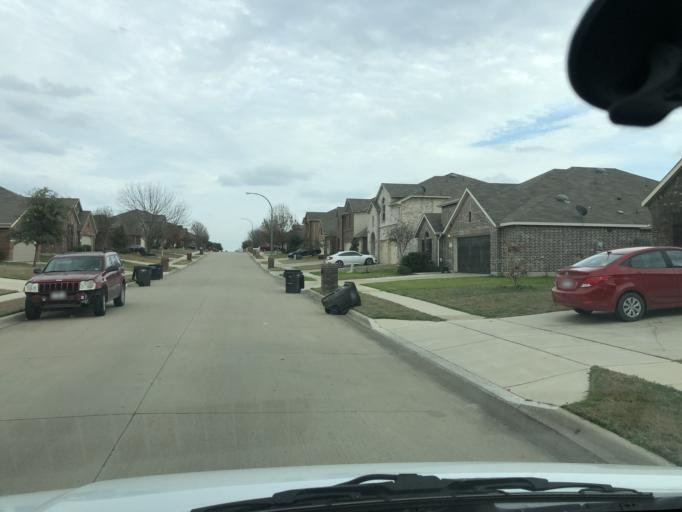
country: US
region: Texas
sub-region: Tarrant County
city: Saginaw
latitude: 32.9067
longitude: -97.3708
